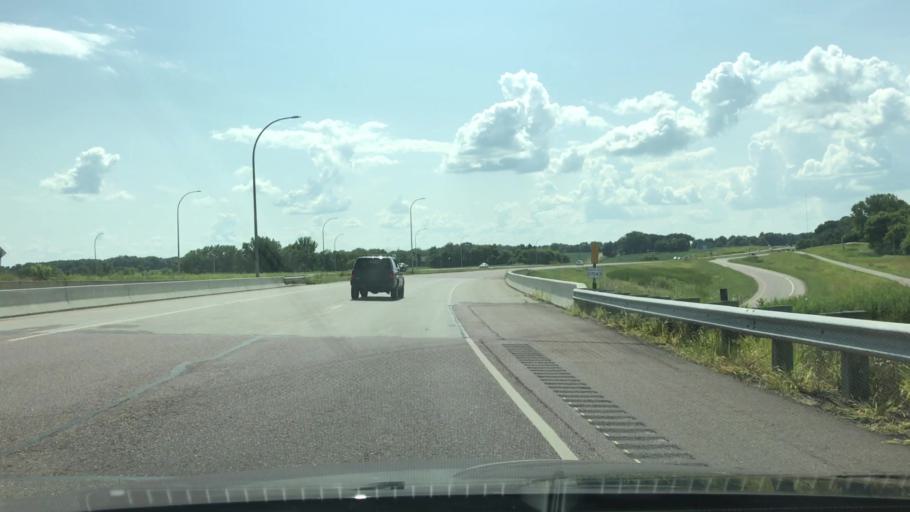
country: US
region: Minnesota
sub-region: Nicollet County
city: North Mankato
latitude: 44.1458
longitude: -94.0836
